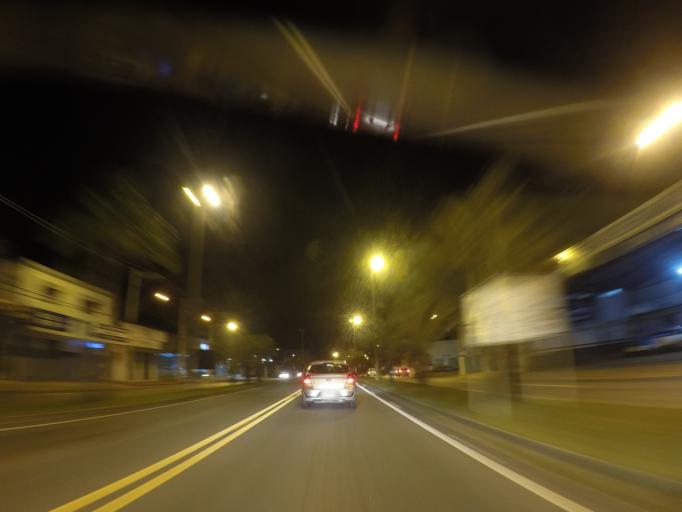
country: BR
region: Espirito Santo
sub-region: Linhares
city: Linhares
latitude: -19.4008
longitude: -40.0618
